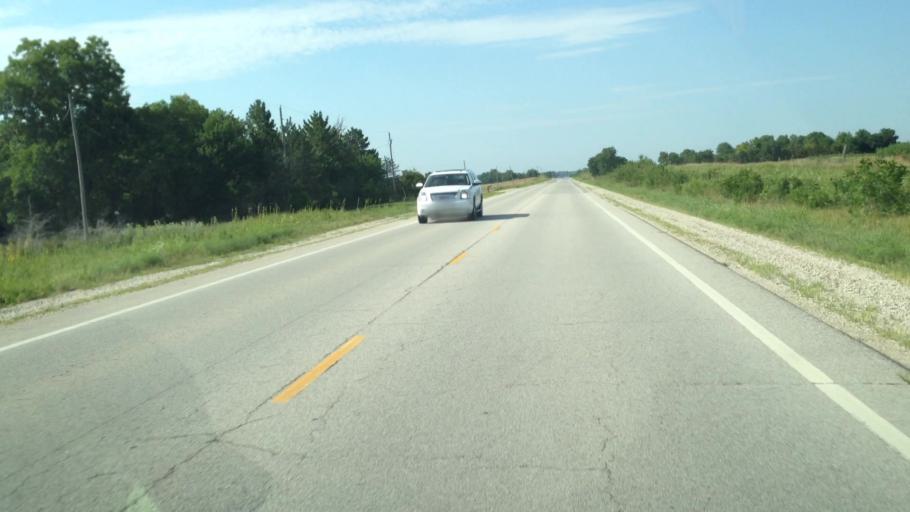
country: US
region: Kansas
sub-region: Neosho County
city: Erie
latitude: 37.4923
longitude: -95.2694
